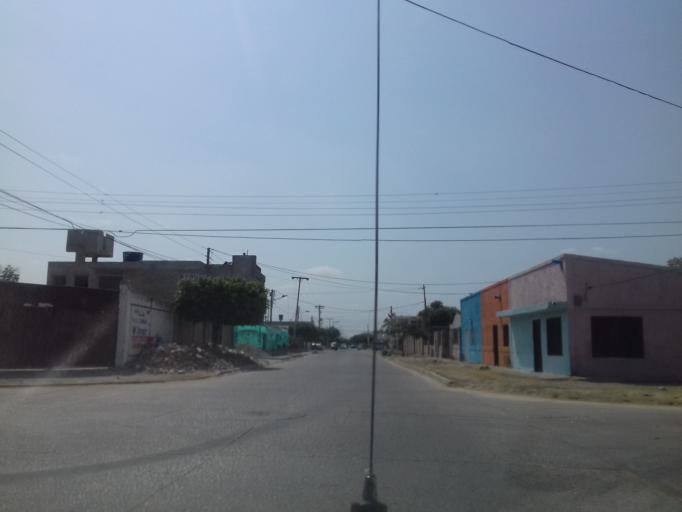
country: CO
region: La Guajira
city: Maicao
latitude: 11.3825
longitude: -72.2445
